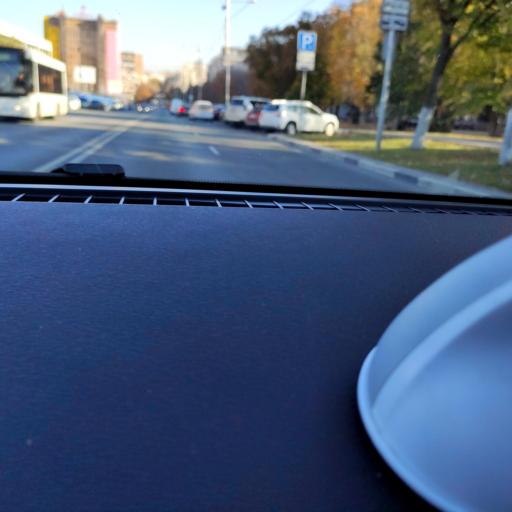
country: RU
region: Samara
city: Samara
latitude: 53.2044
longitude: 50.1149
